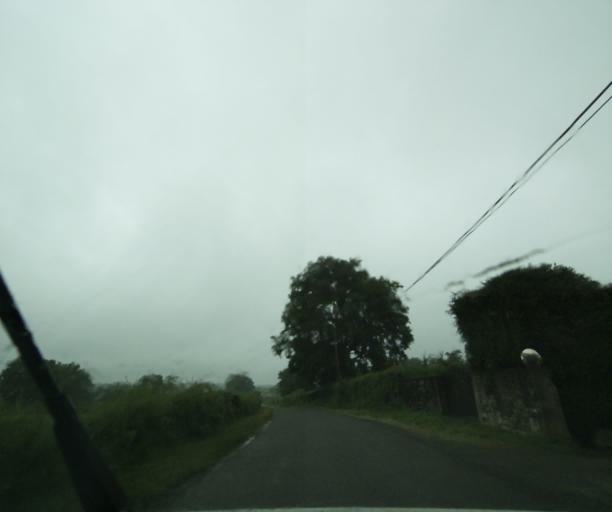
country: FR
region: Bourgogne
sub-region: Departement de Saone-et-Loire
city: Charolles
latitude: 46.4299
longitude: 4.3443
